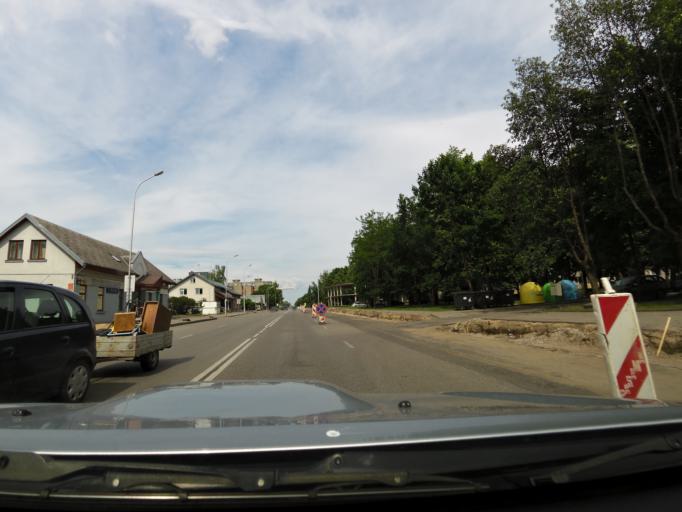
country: LT
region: Marijampoles apskritis
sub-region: Marijampole Municipality
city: Marijampole
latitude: 54.5650
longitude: 23.3568
